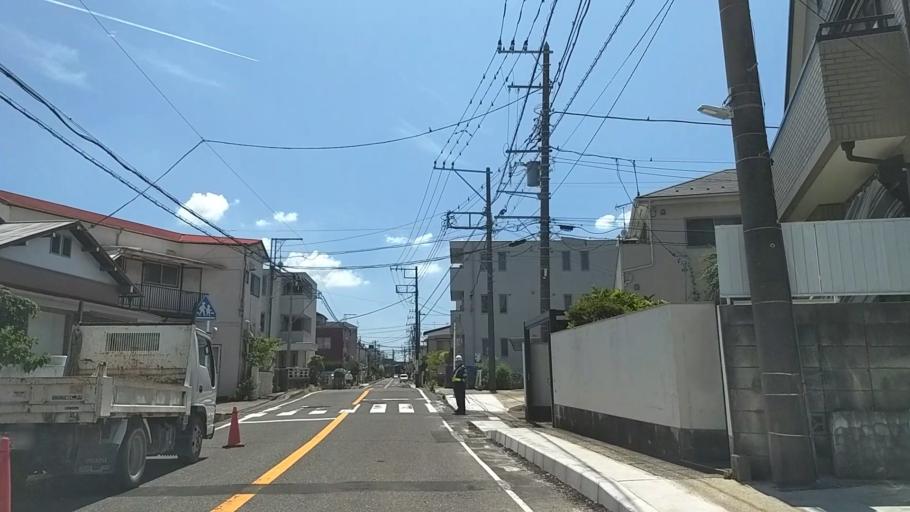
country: JP
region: Kanagawa
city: Zushi
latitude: 35.3019
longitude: 139.5908
